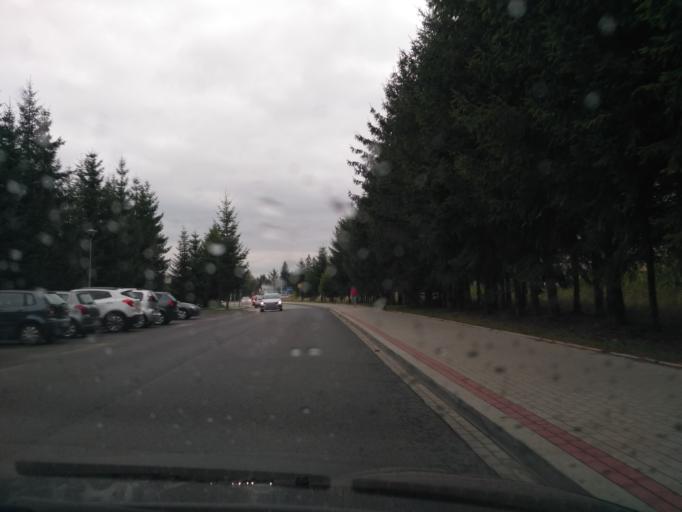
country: PL
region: Subcarpathian Voivodeship
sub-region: Krosno
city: Krosno
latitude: 49.6797
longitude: 21.7766
